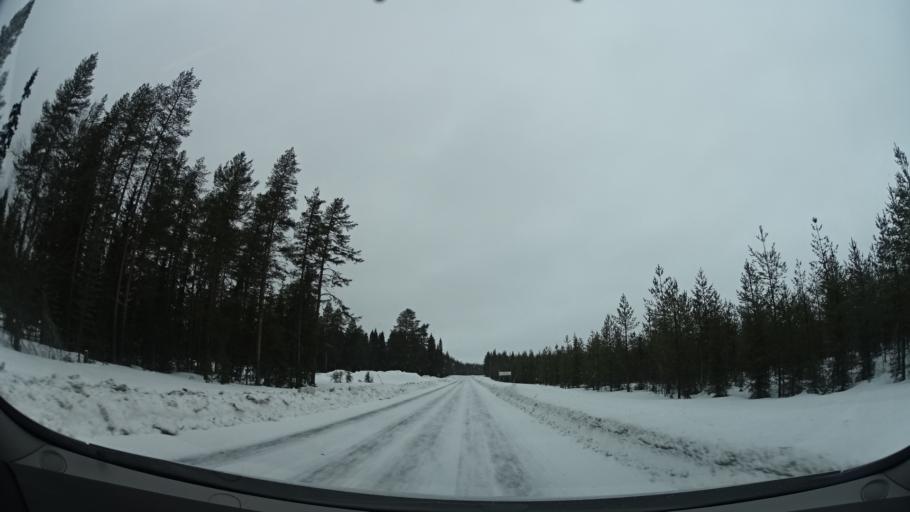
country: SE
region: Vaesterbotten
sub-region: Mala Kommun
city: Mala
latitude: 65.1204
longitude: 18.8780
